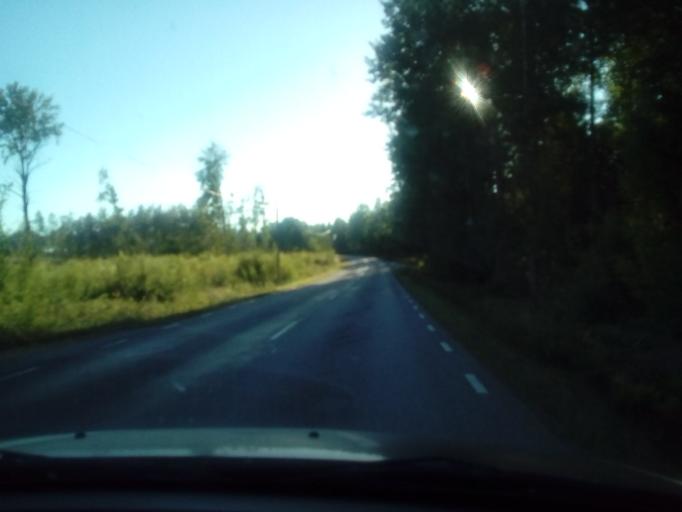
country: SE
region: Kalmar
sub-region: Vasterviks Kommun
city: Ankarsrum
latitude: 57.7887
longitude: 16.3108
